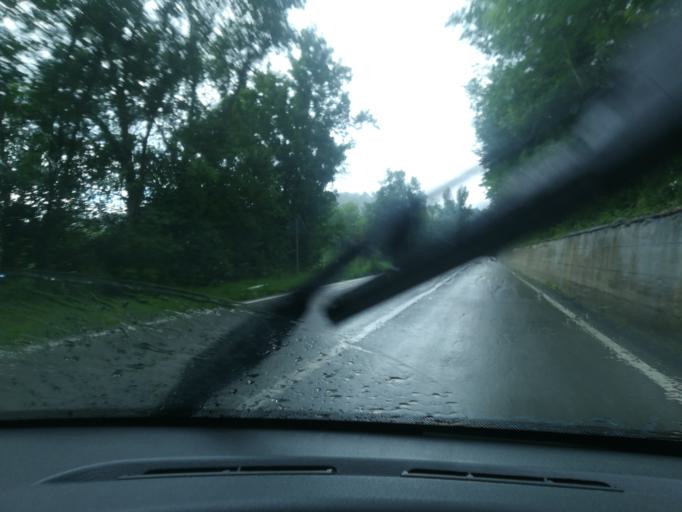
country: IT
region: The Marches
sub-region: Provincia di Macerata
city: Sarnano
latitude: 43.0314
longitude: 13.3108
